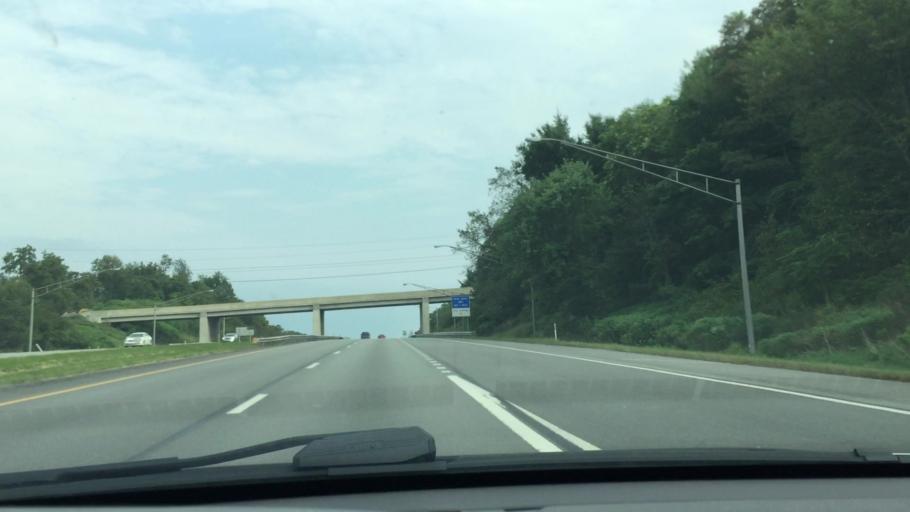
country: US
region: Pennsylvania
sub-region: Beaver County
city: Beaver
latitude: 40.6979
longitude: -80.3621
